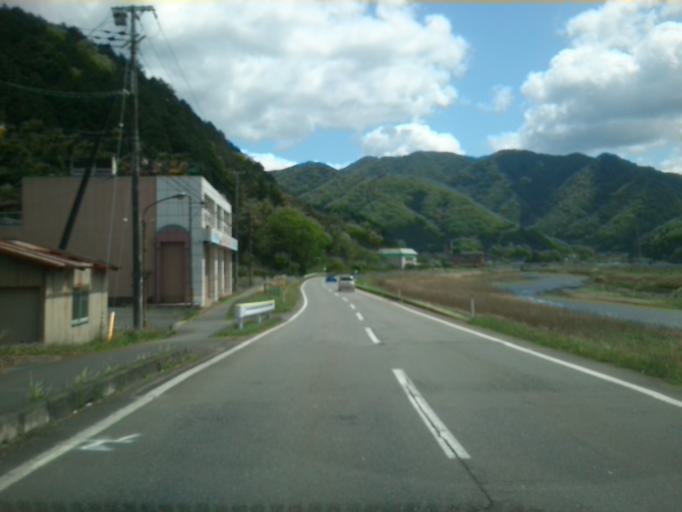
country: JP
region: Hyogo
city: Toyooka
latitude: 35.4558
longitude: 134.8711
